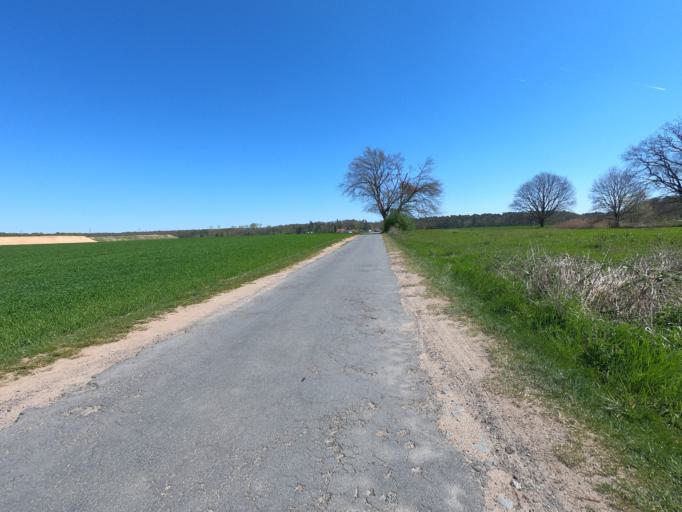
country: DE
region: Hesse
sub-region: Regierungsbezirk Darmstadt
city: Erzhausen
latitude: 49.9227
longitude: 8.6837
